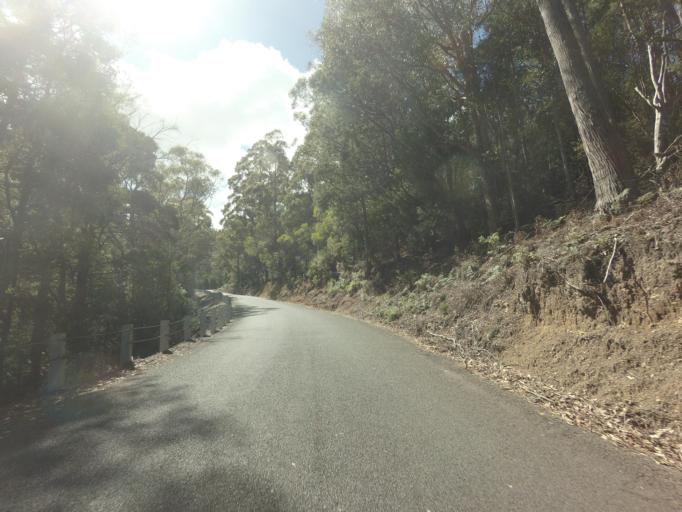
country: AU
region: Tasmania
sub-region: Break O'Day
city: St Helens
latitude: -41.6367
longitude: 148.2432
